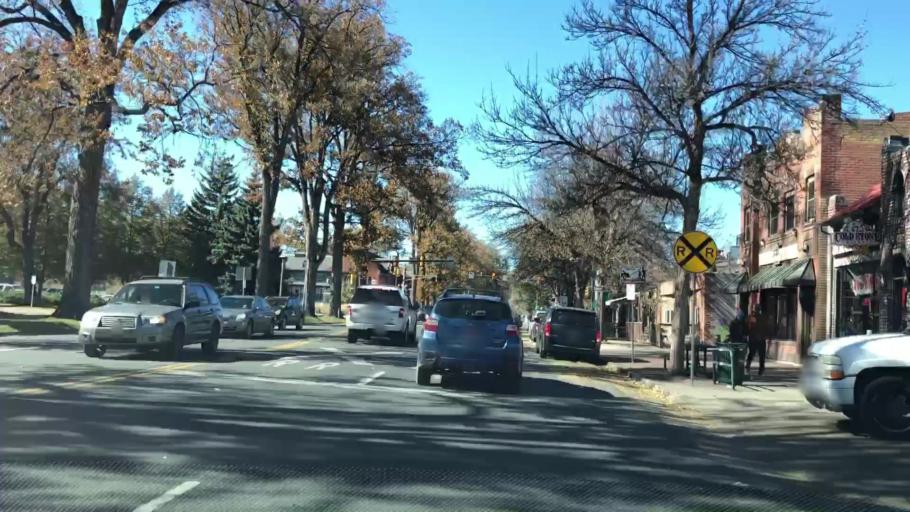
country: US
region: Colorado
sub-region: Larimer County
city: Fort Collins
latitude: 40.5782
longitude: -105.0776
